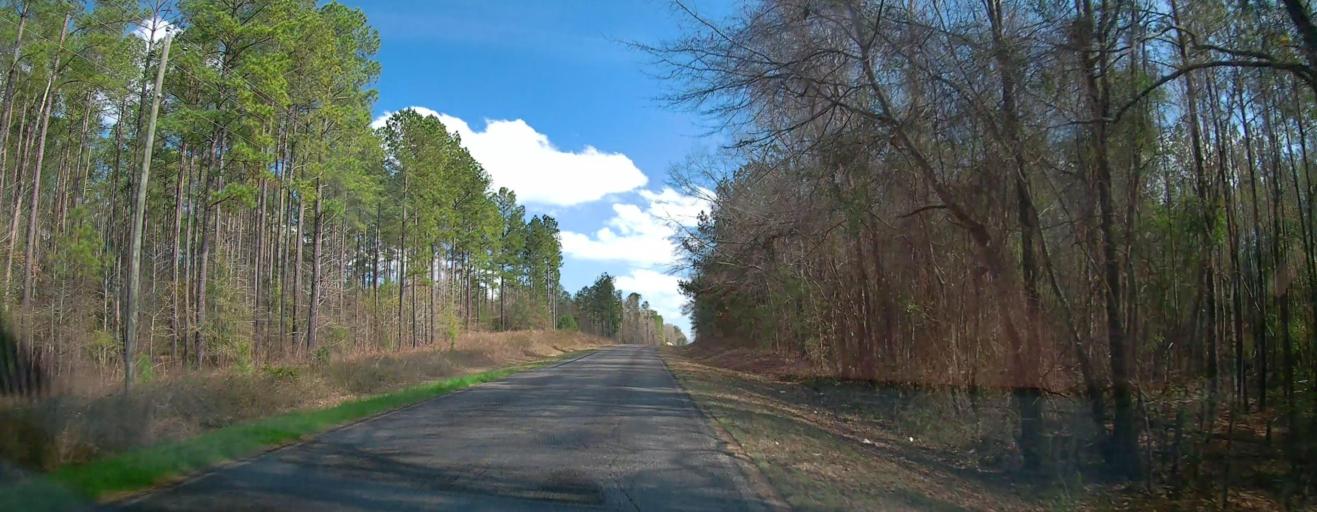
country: US
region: Georgia
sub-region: Twiggs County
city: Jeffersonville
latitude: 32.6626
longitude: -83.2277
